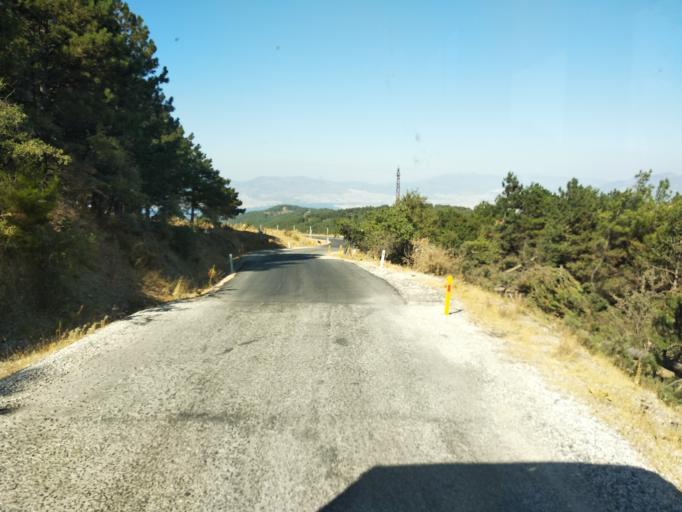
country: TR
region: Izmir
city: Gaziemir
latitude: 38.3185
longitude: 27.0116
